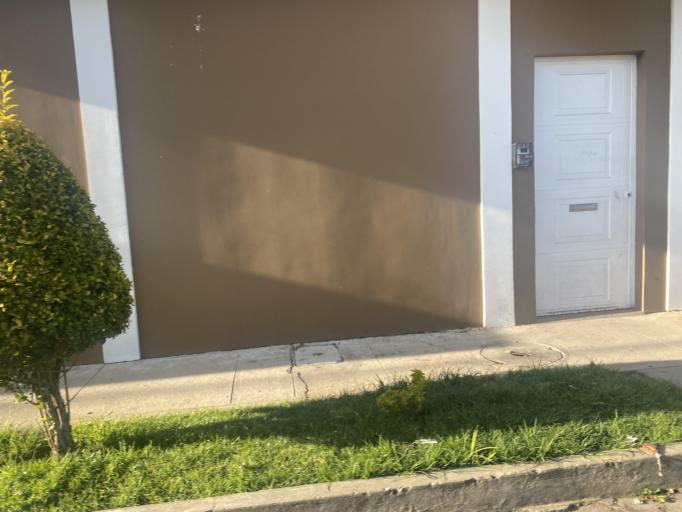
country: GT
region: Quetzaltenango
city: Quetzaltenango
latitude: 14.8582
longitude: -91.5218
